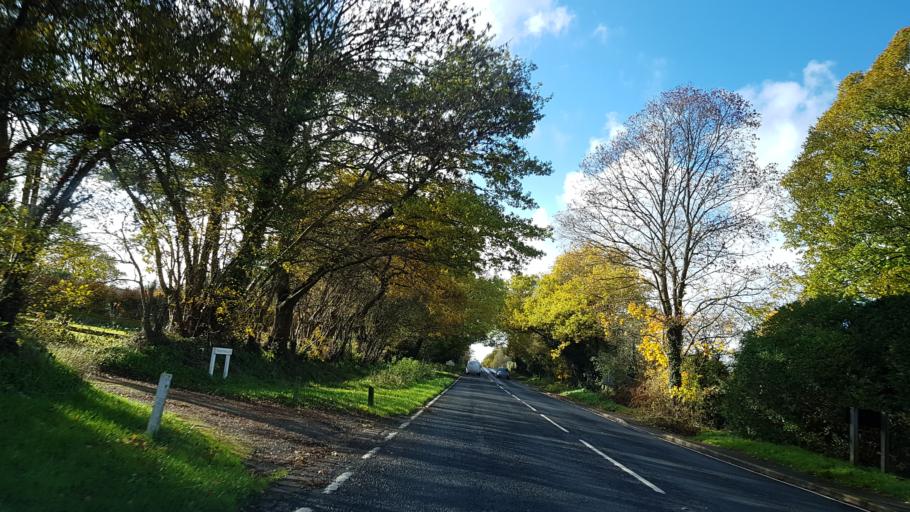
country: GB
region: England
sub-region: Surrey
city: Milford
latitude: 51.1653
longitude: -0.6535
